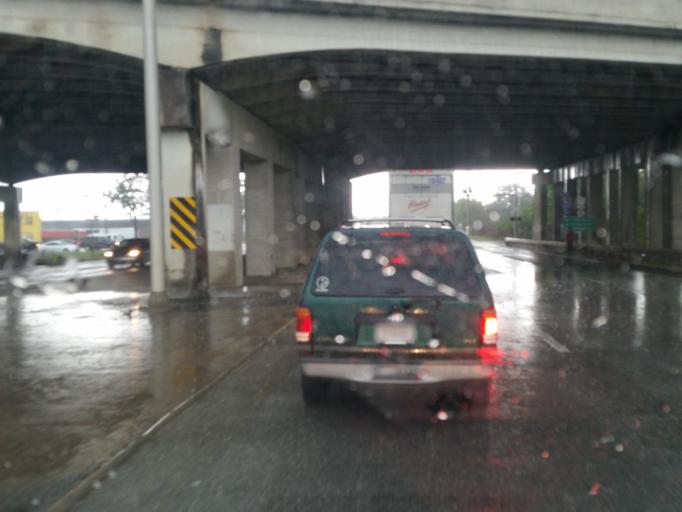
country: US
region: Alabama
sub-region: Mobile County
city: Prichard
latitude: 30.7072
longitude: -88.1228
